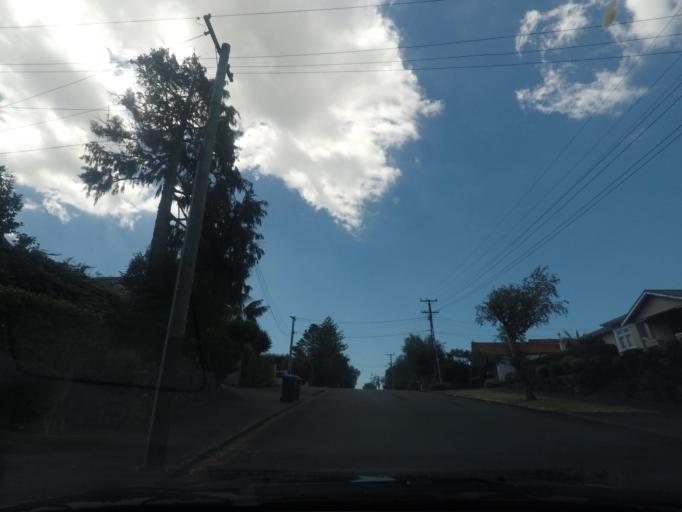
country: NZ
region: Auckland
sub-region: Auckland
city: Auckland
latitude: -36.8883
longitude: 174.7669
